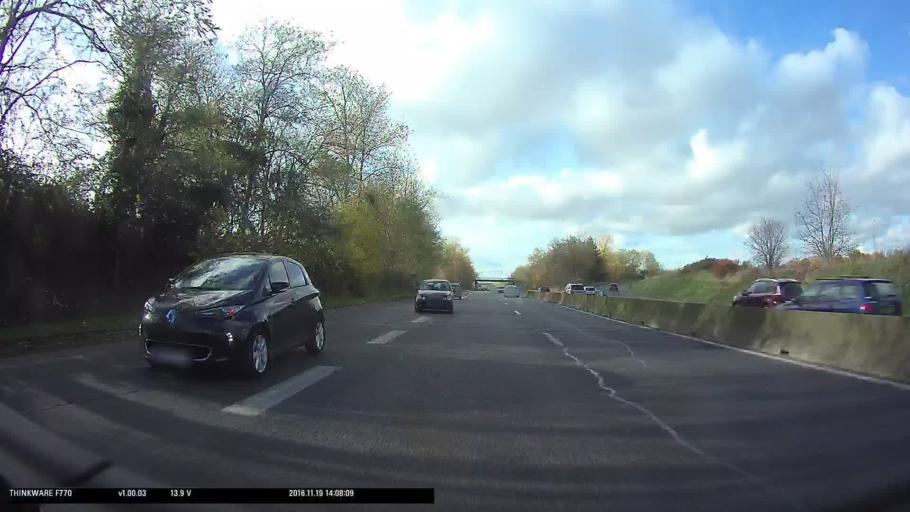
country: FR
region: Ile-de-France
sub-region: Departement du Val-d'Oise
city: Vaureal
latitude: 49.0582
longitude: 2.0343
